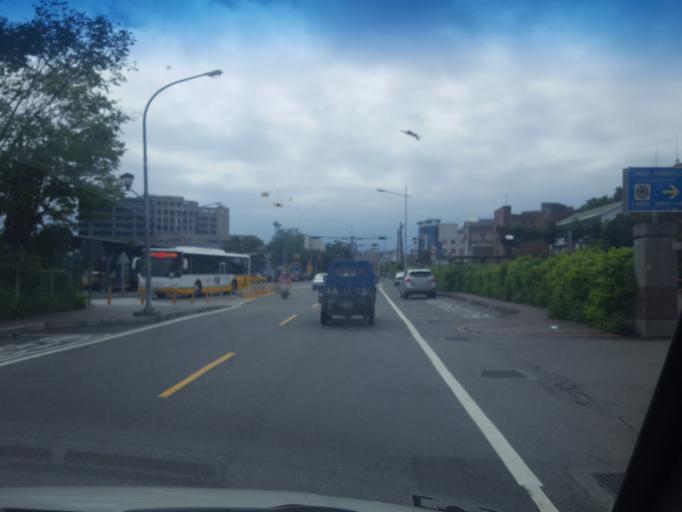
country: TW
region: Taiwan
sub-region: Yilan
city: Yilan
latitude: 24.7530
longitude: 121.7589
